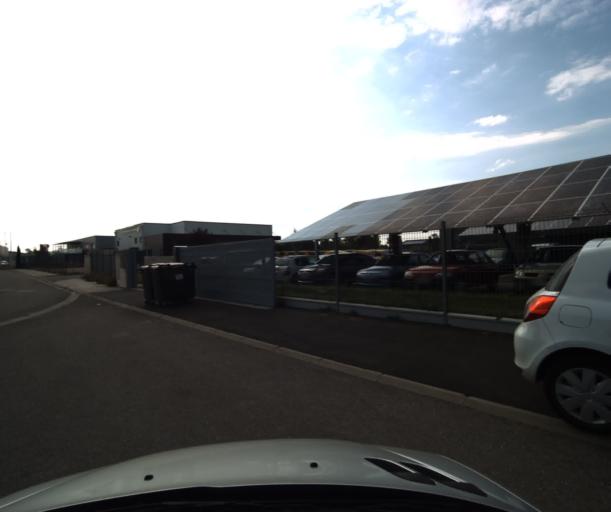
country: FR
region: Midi-Pyrenees
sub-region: Departement de la Haute-Garonne
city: Saint-Lys
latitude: 43.5133
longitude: 1.1999
